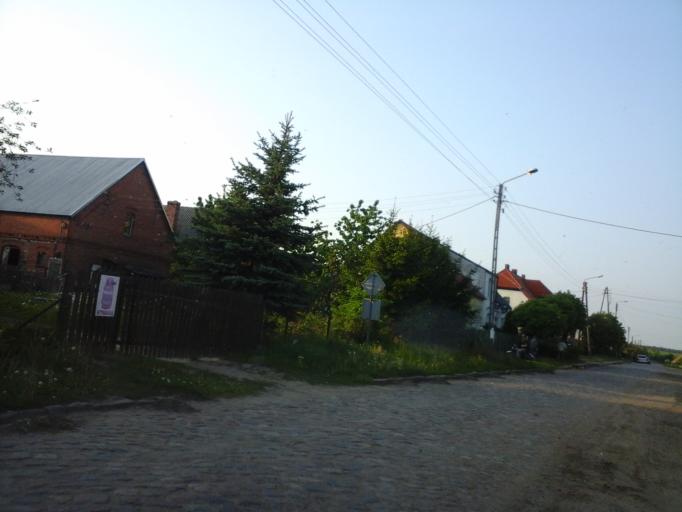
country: PL
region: West Pomeranian Voivodeship
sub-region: Powiat choszczenski
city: Bierzwnik
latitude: 52.9908
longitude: 15.6308
